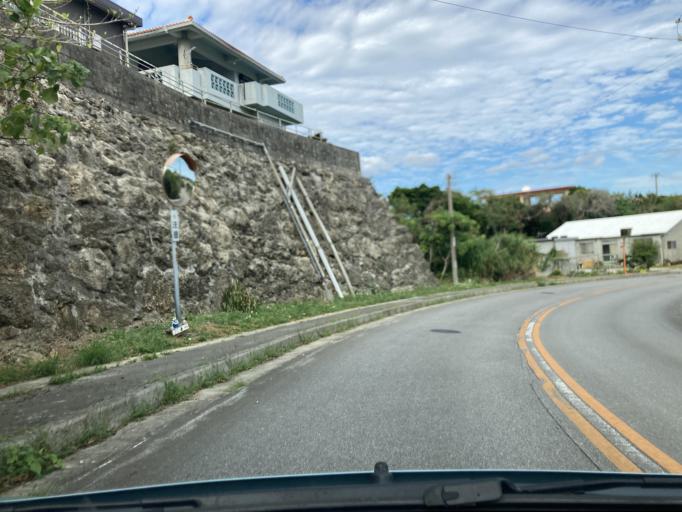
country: JP
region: Okinawa
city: Ishikawa
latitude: 26.4351
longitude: 127.7778
